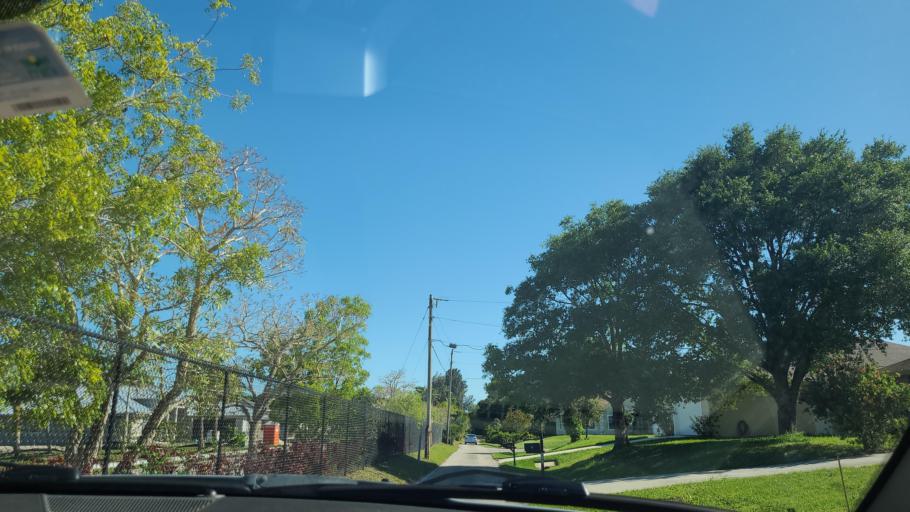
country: US
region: Florida
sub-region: Indian River County
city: Sebastian
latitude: 27.7576
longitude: -80.4784
